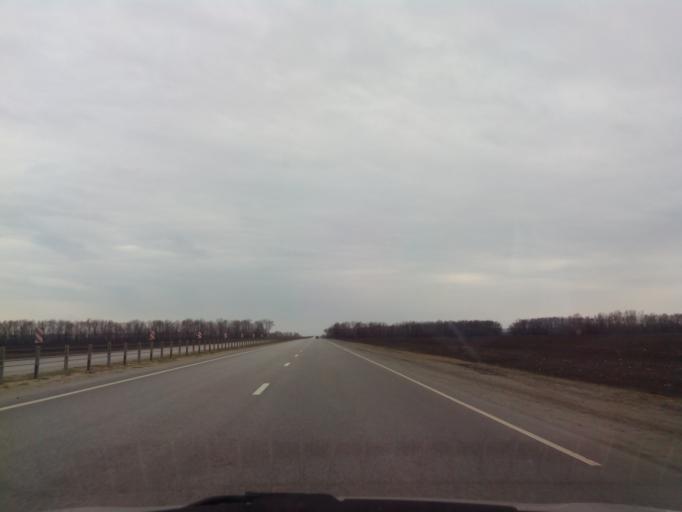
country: RU
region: Tambov
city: Zavoronezhskoye
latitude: 52.8934
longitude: 40.6888
